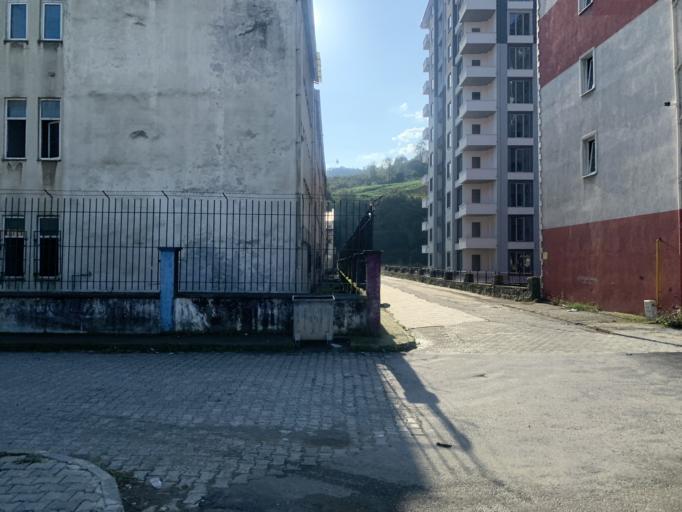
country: TR
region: Trabzon
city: Of
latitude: 40.9407
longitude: 40.2694
